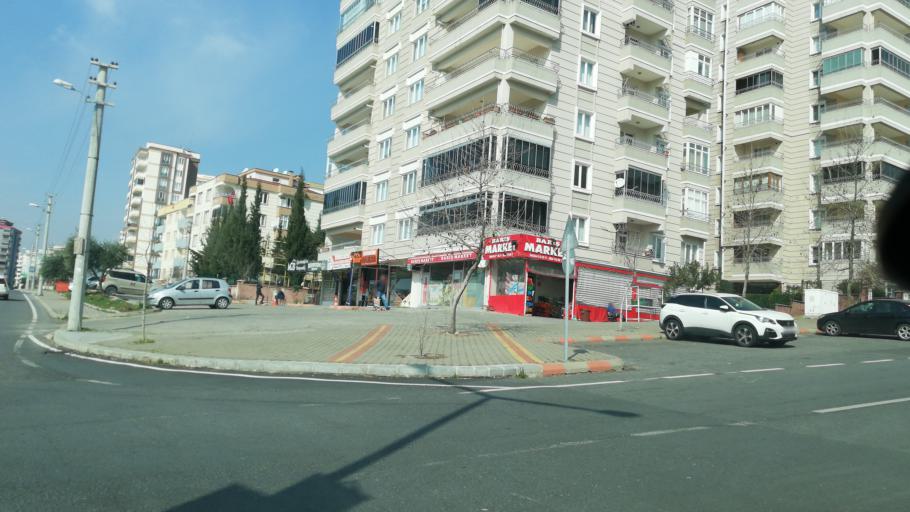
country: TR
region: Kahramanmaras
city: Kahramanmaras
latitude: 37.5890
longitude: 36.8628
